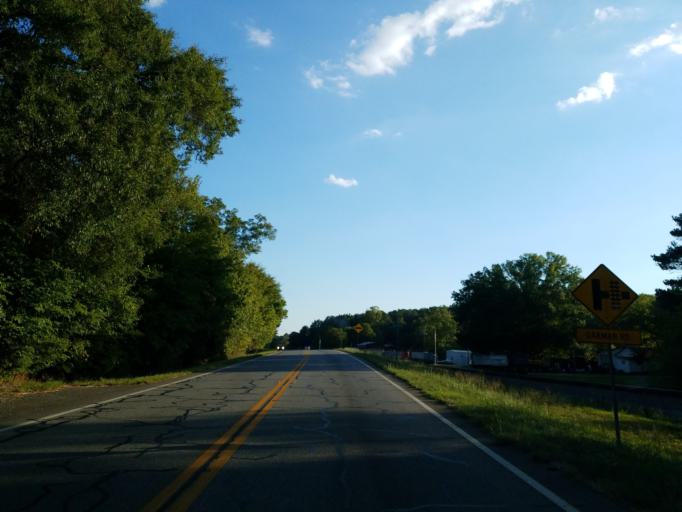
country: US
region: Georgia
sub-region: Murray County
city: Chatsworth
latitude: 34.5683
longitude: -84.7080
